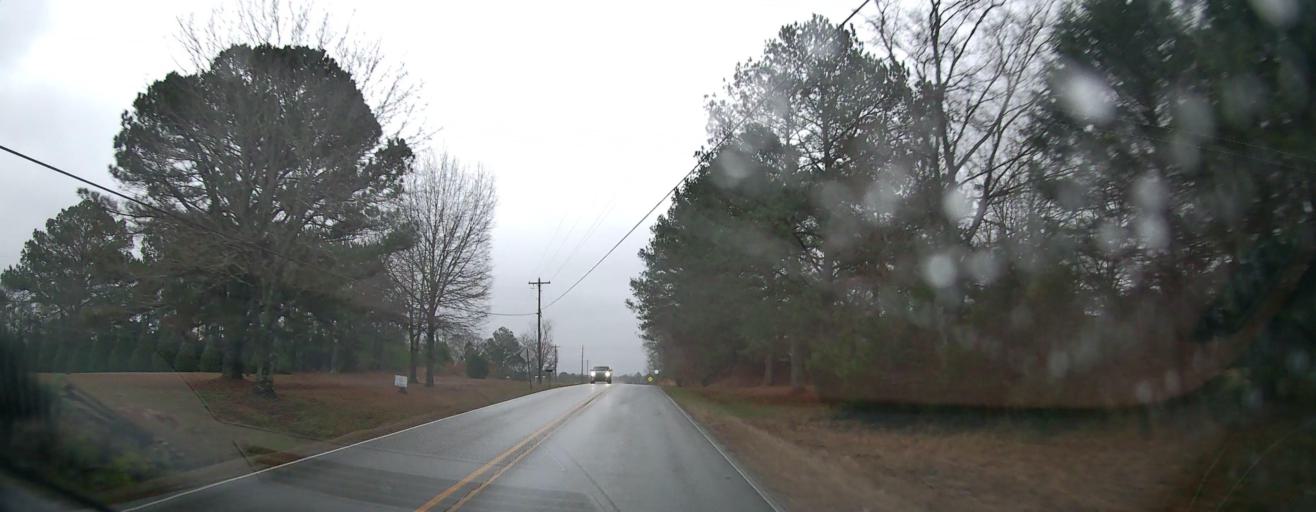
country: US
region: Alabama
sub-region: Morgan County
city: Hartselle
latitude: 34.4125
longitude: -86.9052
